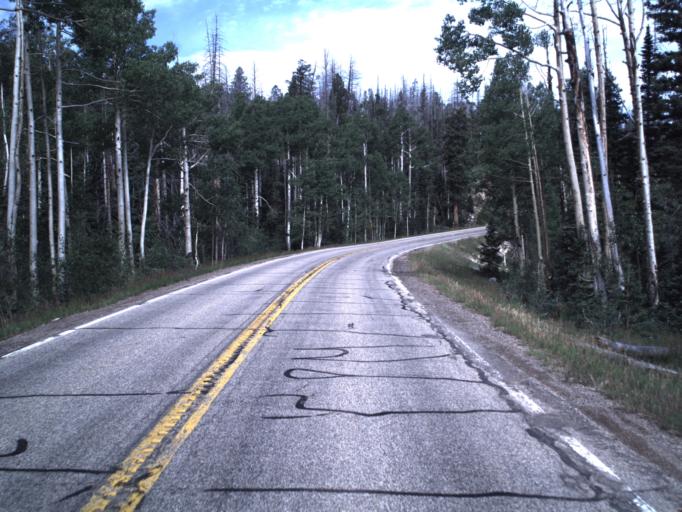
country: US
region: Utah
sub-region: Iron County
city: Parowan
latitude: 37.5336
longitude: -112.7709
